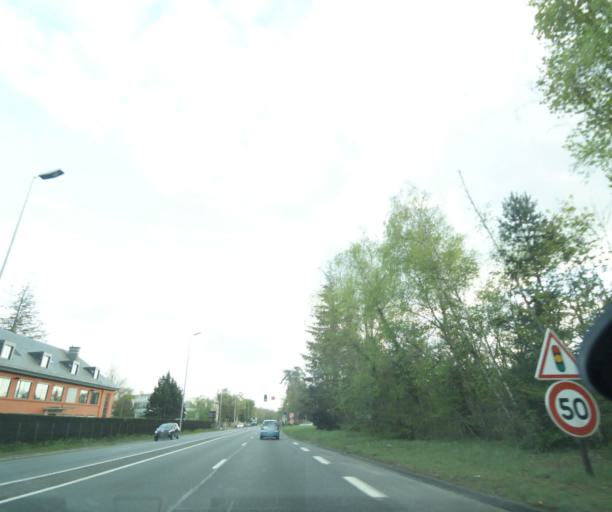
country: FR
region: Ile-de-France
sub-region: Departement de Seine-et-Marne
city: Fontainebleau
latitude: 48.4065
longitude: 2.6867
